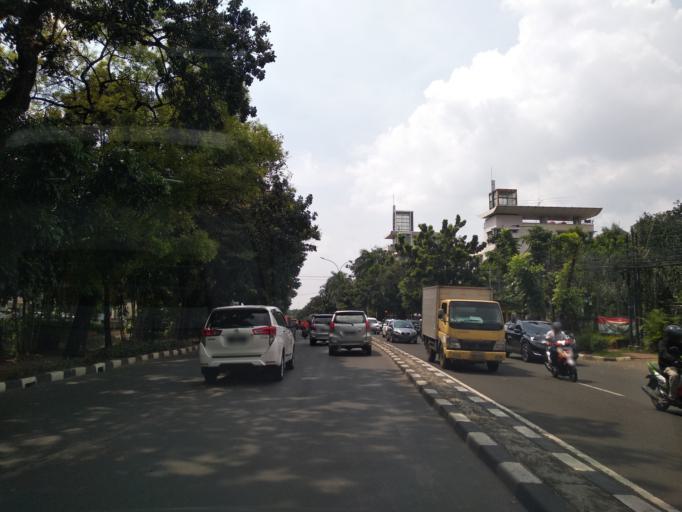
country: ID
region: Jakarta Raya
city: Jakarta
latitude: -6.2274
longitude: 106.8474
